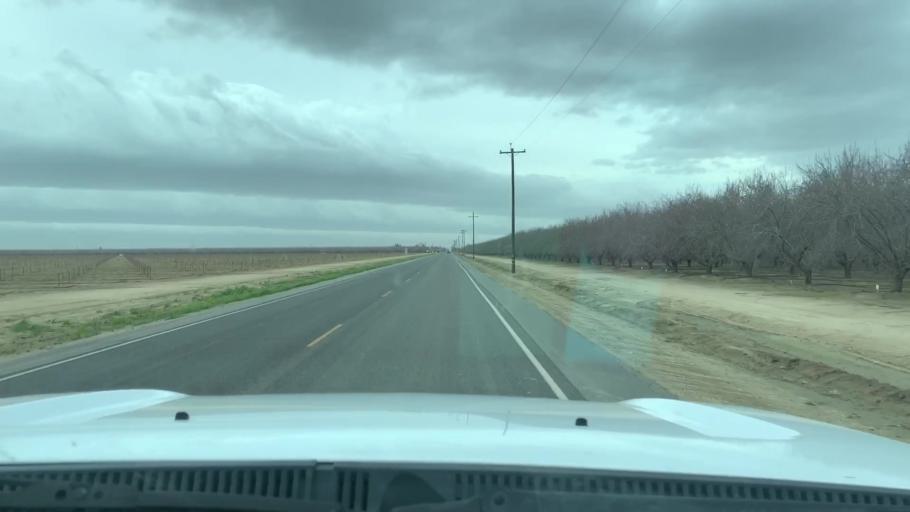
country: US
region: California
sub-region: Kern County
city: Wasco
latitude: 35.5581
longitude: -119.3050
